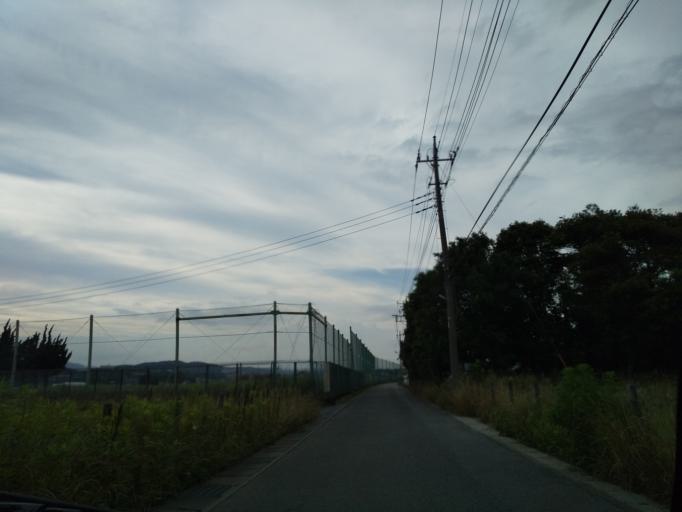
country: JP
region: Kanagawa
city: Zama
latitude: 35.4746
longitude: 139.3602
